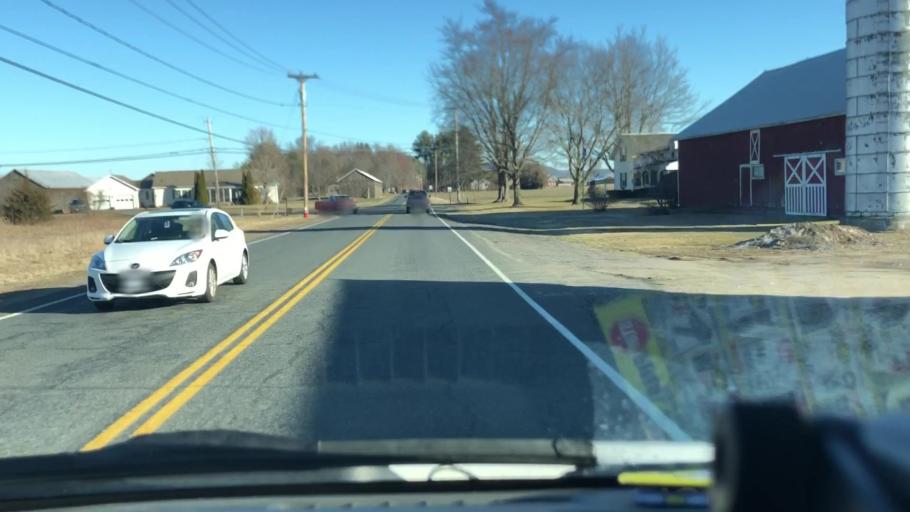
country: US
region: Massachusetts
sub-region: Hampshire County
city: North Amherst
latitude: 42.3881
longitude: -72.5478
